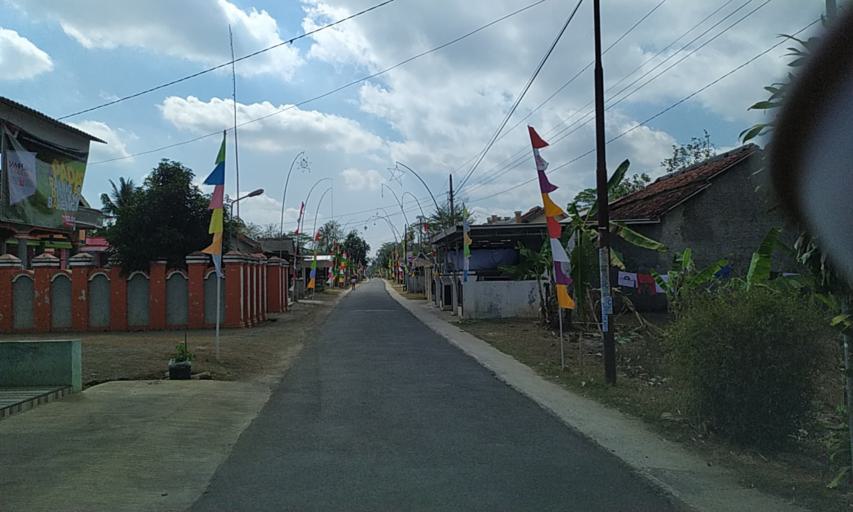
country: ID
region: Central Java
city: Kroya
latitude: -7.6277
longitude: 109.2783
